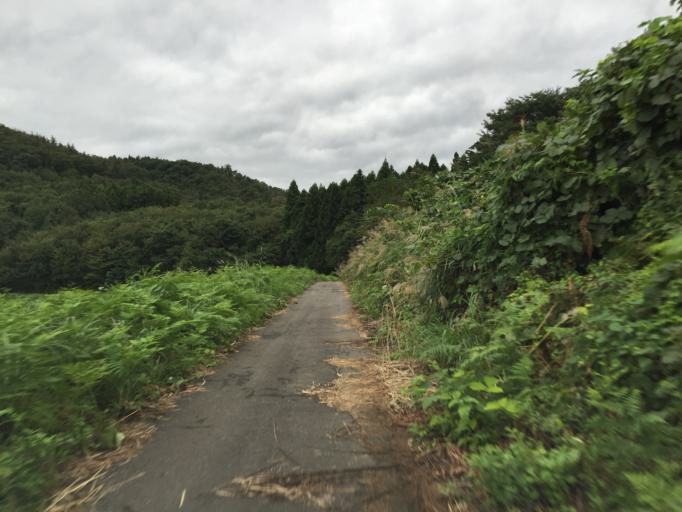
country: JP
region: Fukushima
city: Hobaramachi
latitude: 37.7644
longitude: 140.5291
